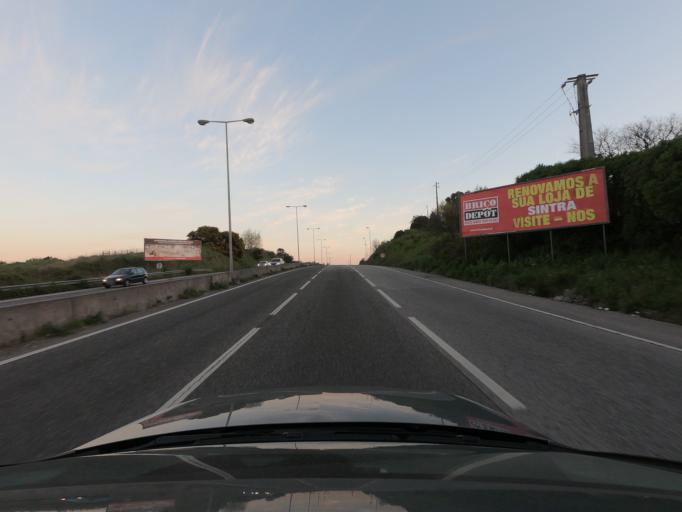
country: PT
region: Lisbon
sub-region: Sintra
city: Queluz
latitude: 38.7514
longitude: -9.2643
